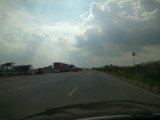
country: IN
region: Karnataka
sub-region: Kolar
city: Kolar
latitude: 13.1351
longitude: 78.0165
